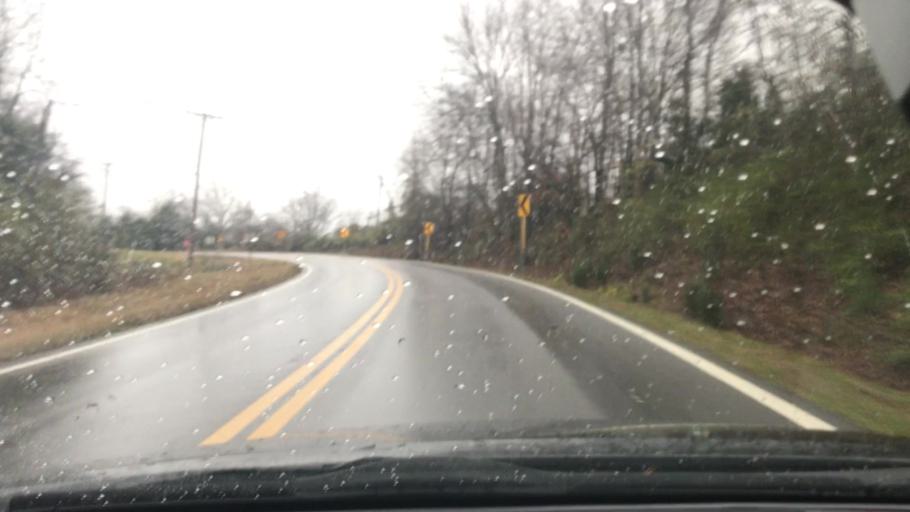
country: US
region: Tennessee
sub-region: Cheatham County
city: Ashland City
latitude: 36.2763
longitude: -87.1202
